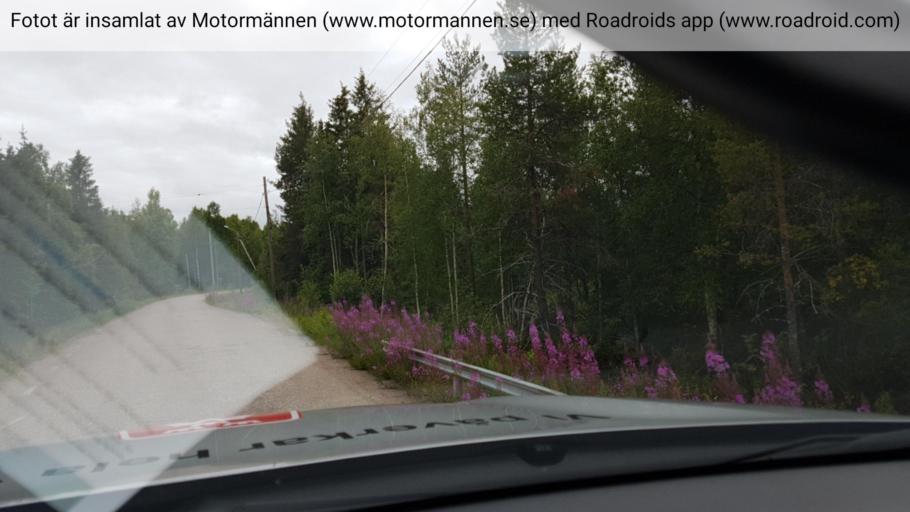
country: SE
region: Norrbotten
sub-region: Pajala Kommun
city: Pajala
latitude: 67.1764
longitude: 22.6538
